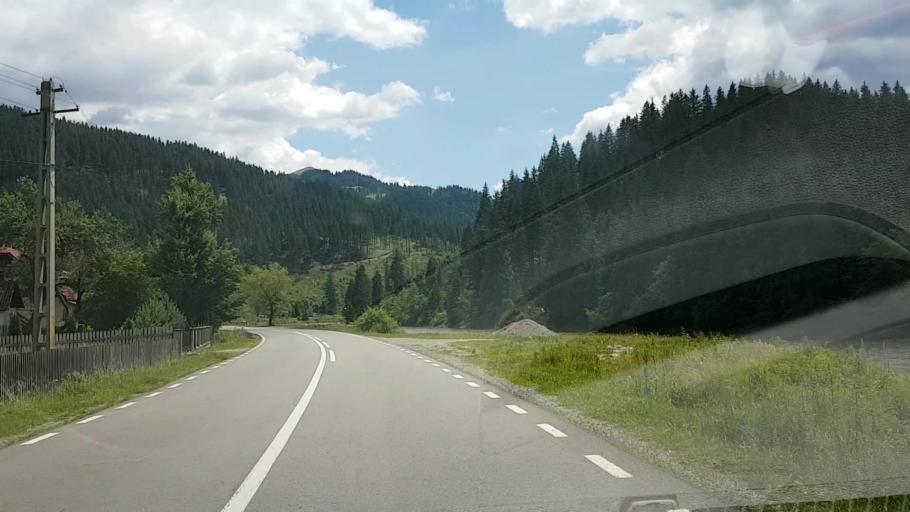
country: RO
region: Suceava
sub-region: Comuna Crucea
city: Crucea
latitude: 47.3583
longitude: 25.6098
